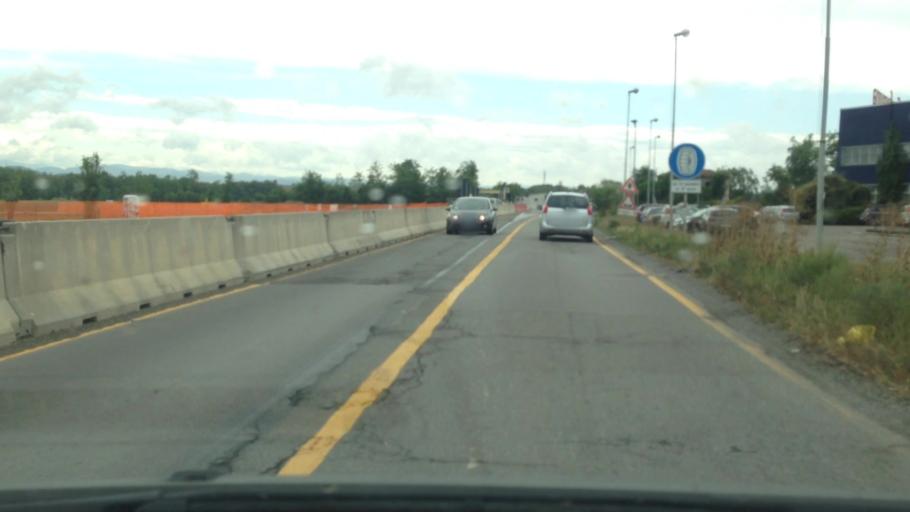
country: IT
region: Piedmont
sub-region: Provincia di Alessandria
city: Tortona
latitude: 44.9037
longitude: 8.8379
